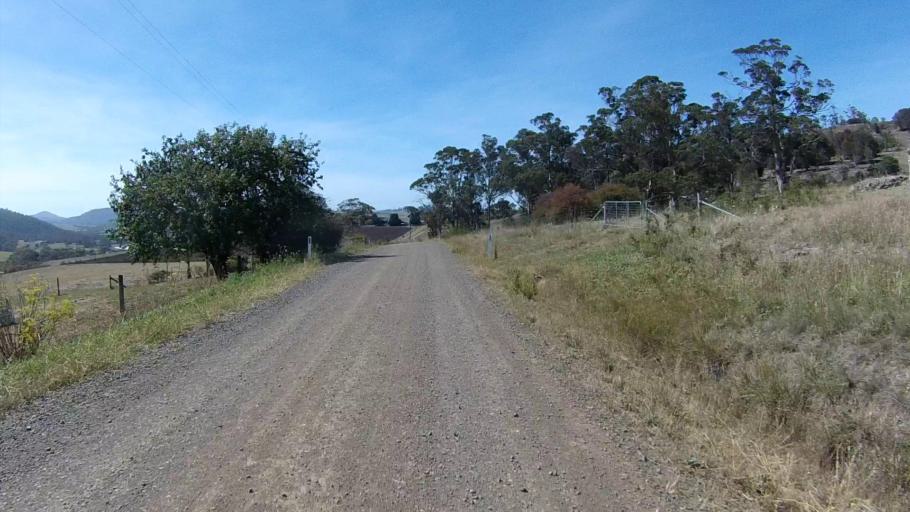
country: AU
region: Tasmania
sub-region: Sorell
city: Sorell
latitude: -42.7448
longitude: 147.6026
